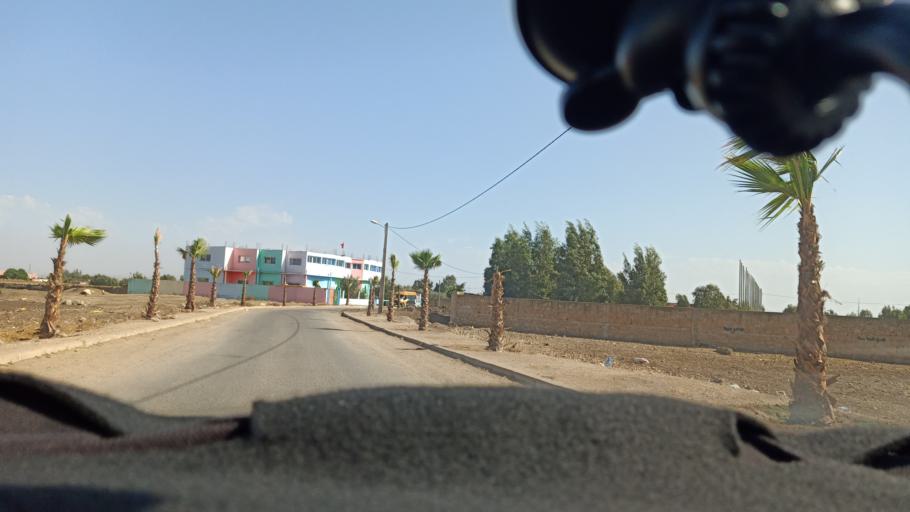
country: MA
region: Doukkala-Abda
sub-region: Safi
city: Youssoufia
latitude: 32.3494
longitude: -8.8348
